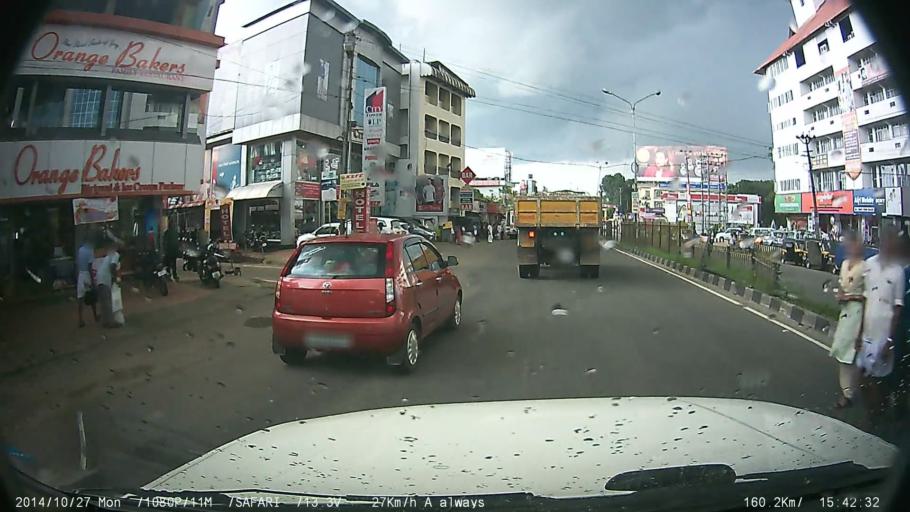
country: IN
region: Kerala
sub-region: Ernakulam
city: Angamali
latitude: 10.1950
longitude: 76.3861
